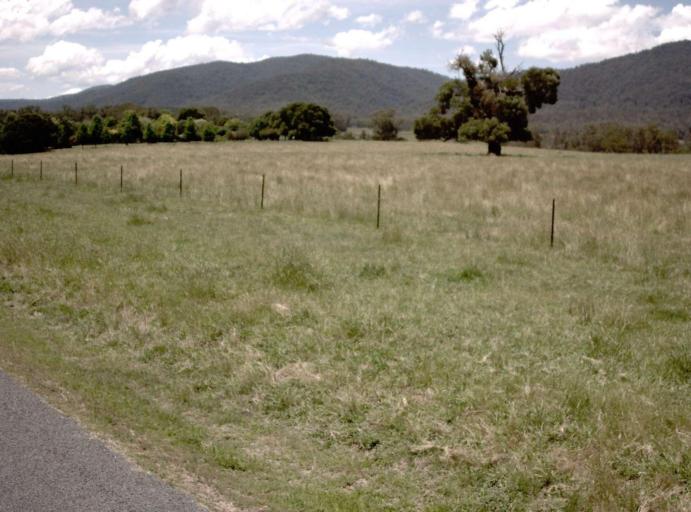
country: AU
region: New South Wales
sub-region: Bombala
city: Bombala
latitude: -37.4181
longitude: 149.0095
